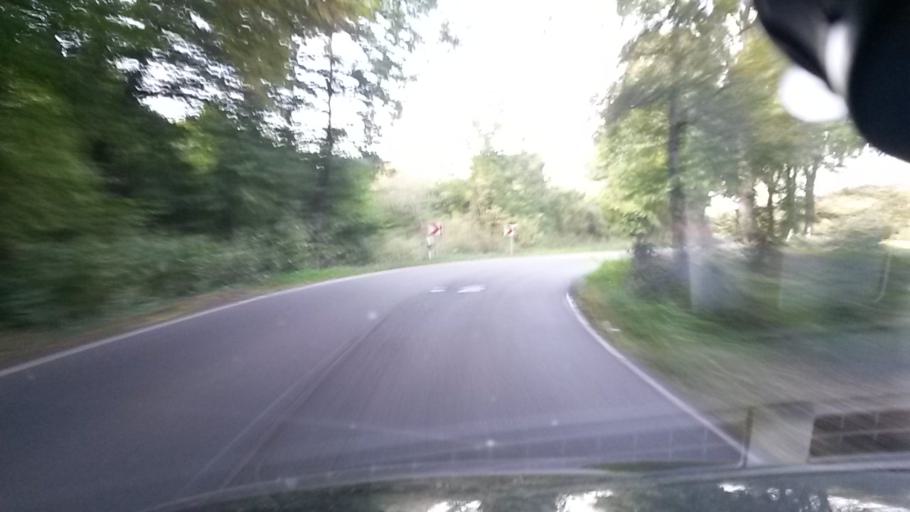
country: DE
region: North Rhine-Westphalia
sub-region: Regierungsbezirk Koln
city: Marienheide
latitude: 51.0655
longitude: 7.5132
